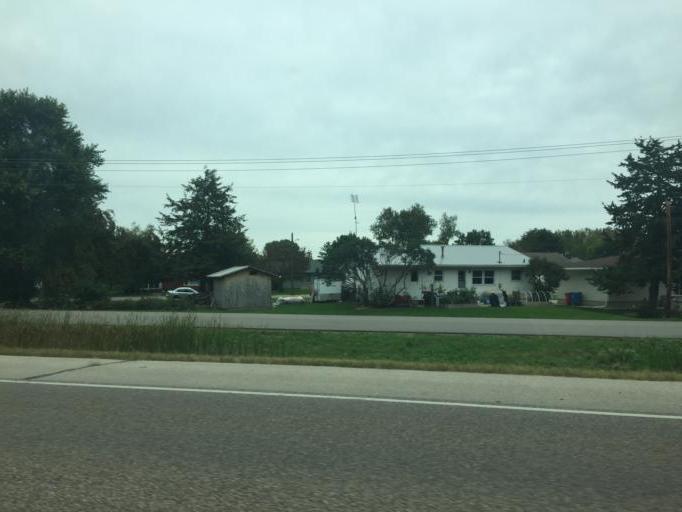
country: US
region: Minnesota
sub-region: Winona County
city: Goodview
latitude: 44.0462
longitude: -91.6730
